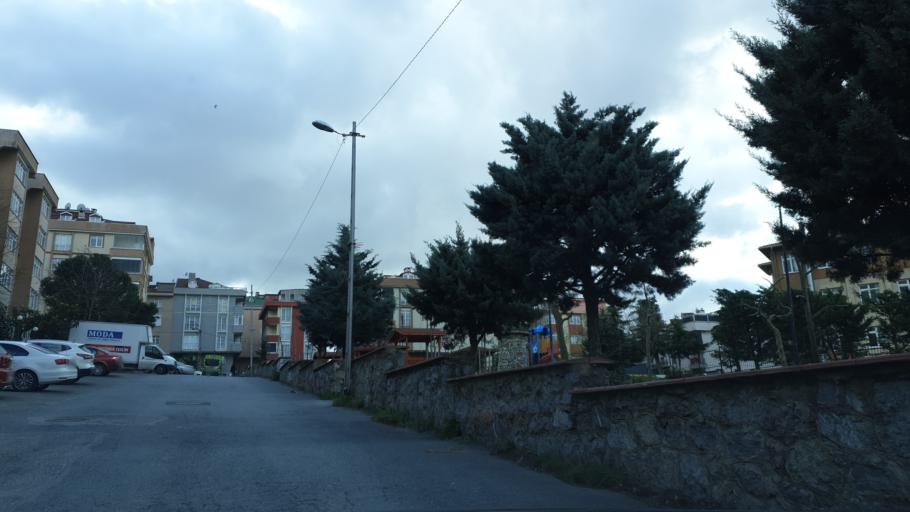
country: TR
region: Istanbul
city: Pendik
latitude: 40.9061
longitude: 29.2479
